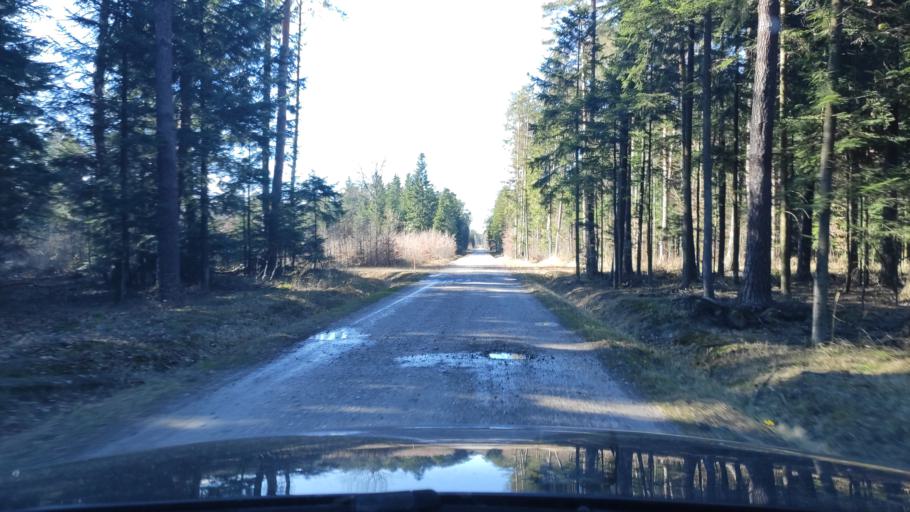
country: PL
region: Masovian Voivodeship
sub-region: Powiat radomski
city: Jedlnia-Letnisko
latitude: 51.4675
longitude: 21.3118
